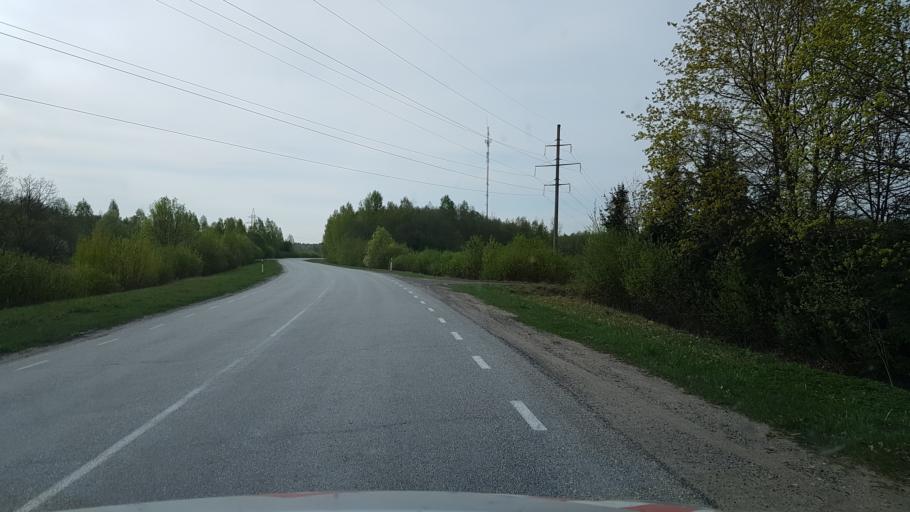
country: EE
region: Paernumaa
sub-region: Audru vald
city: Audru
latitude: 58.4214
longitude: 24.3086
